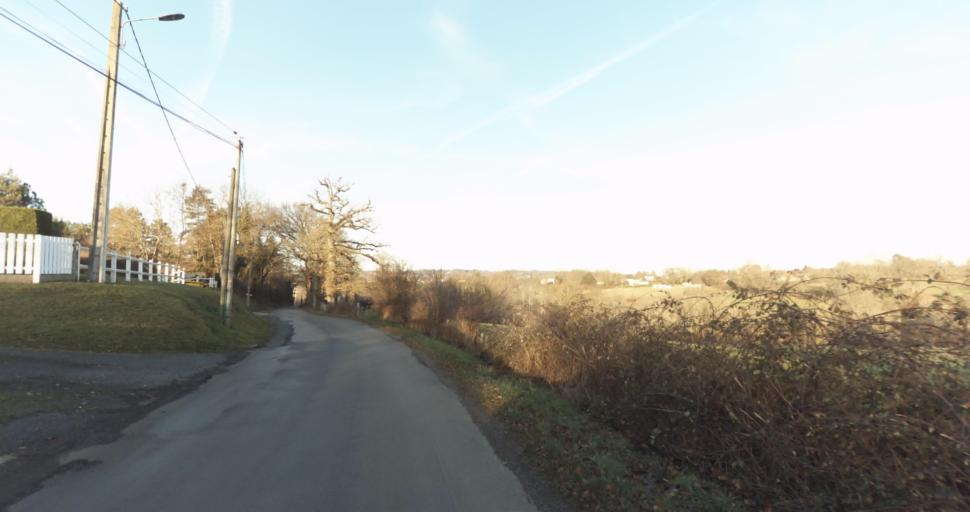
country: FR
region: Limousin
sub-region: Departement de la Haute-Vienne
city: Aixe-sur-Vienne
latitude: 45.7858
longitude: 1.1434
